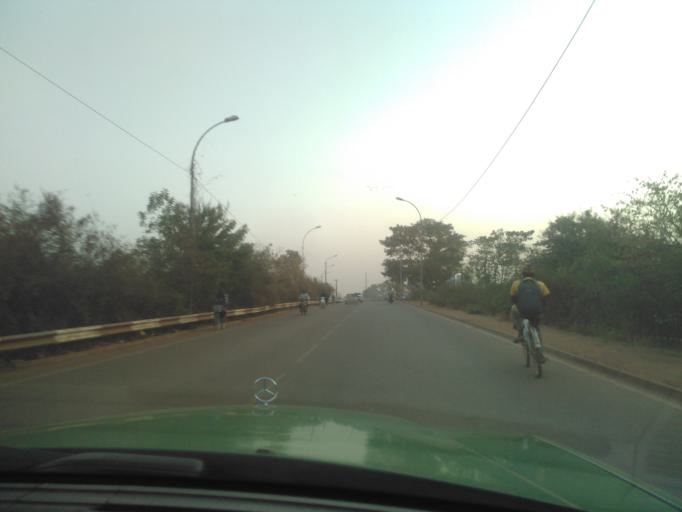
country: BF
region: Centre
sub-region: Kadiogo Province
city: Ouagadougou
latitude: 12.3918
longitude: -1.5012
